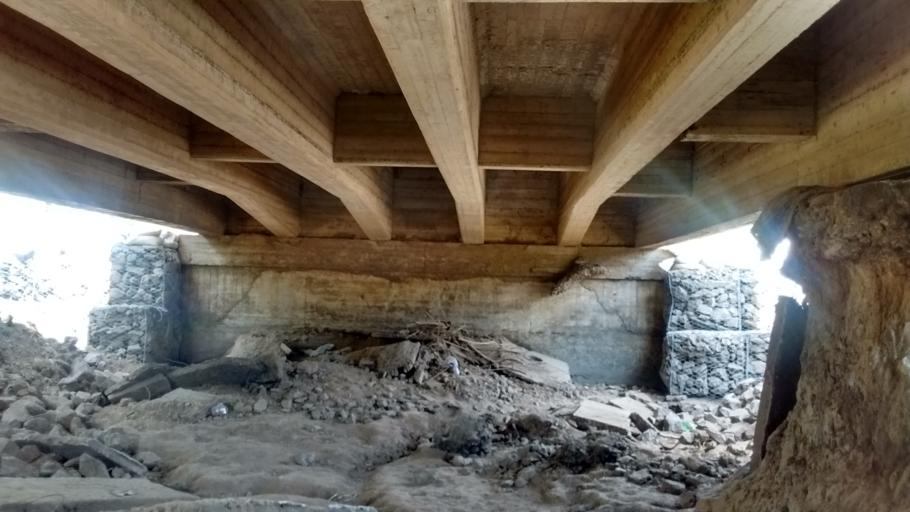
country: AR
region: Cordoba
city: General Roca
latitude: -32.7337
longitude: -61.8377
